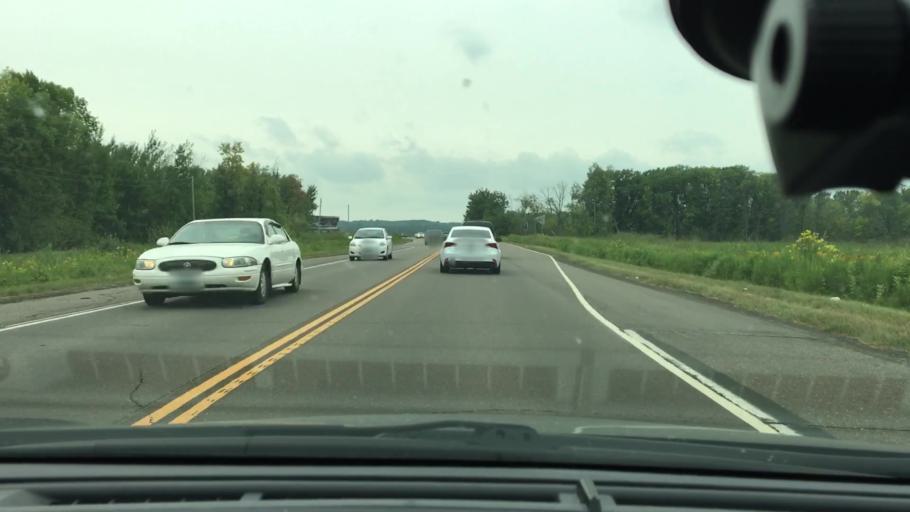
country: US
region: Minnesota
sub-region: Mille Lacs County
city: Vineland
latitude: 46.1689
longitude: -93.7591
